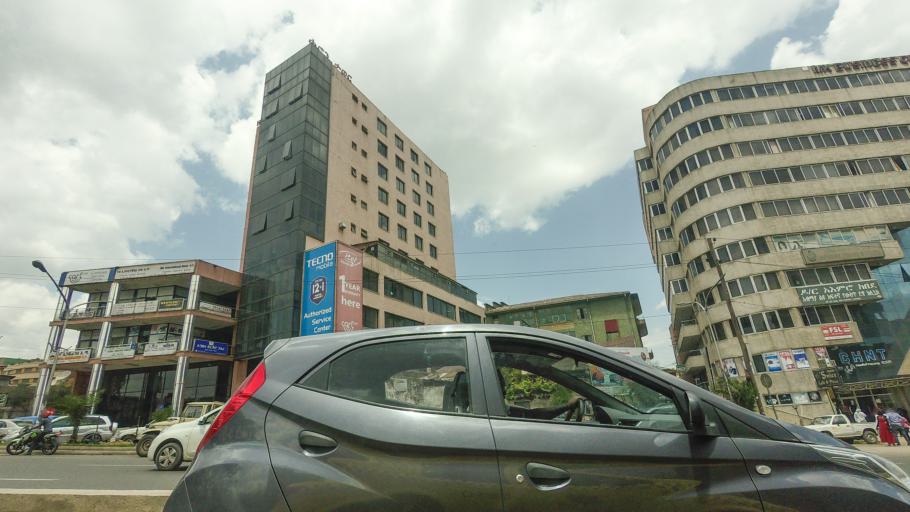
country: ET
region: Adis Abeba
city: Addis Ababa
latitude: 9.0285
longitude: 38.7515
